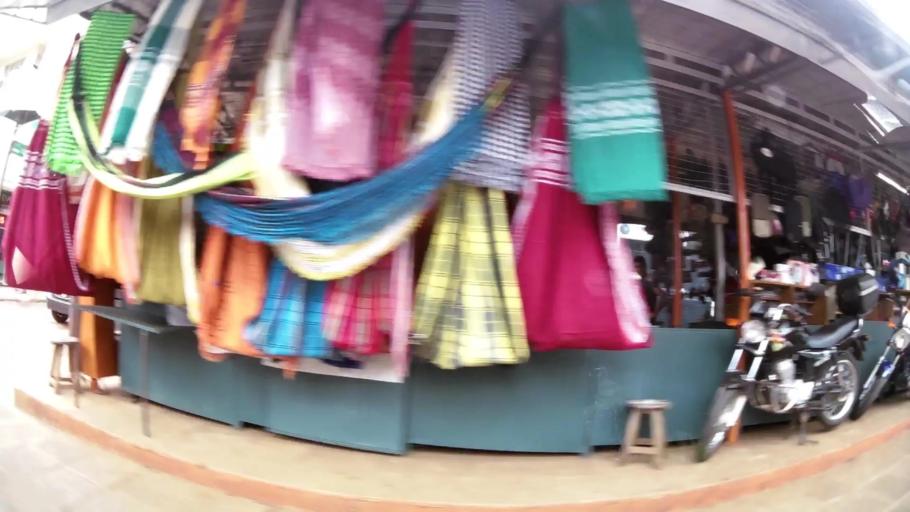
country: PY
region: Alto Parana
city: Ciudad del Este
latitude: -25.5097
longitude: -54.6121
